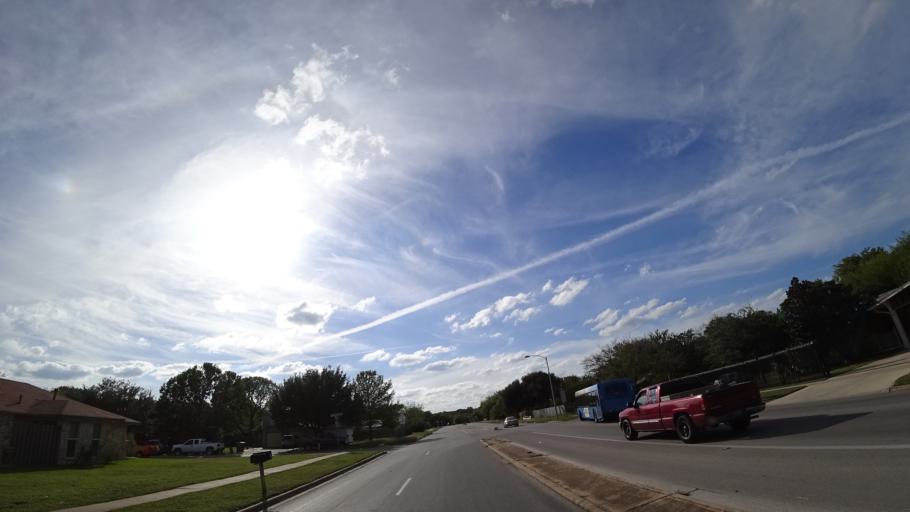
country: US
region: Texas
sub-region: Travis County
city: Onion Creek
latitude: 30.1935
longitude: -97.7521
